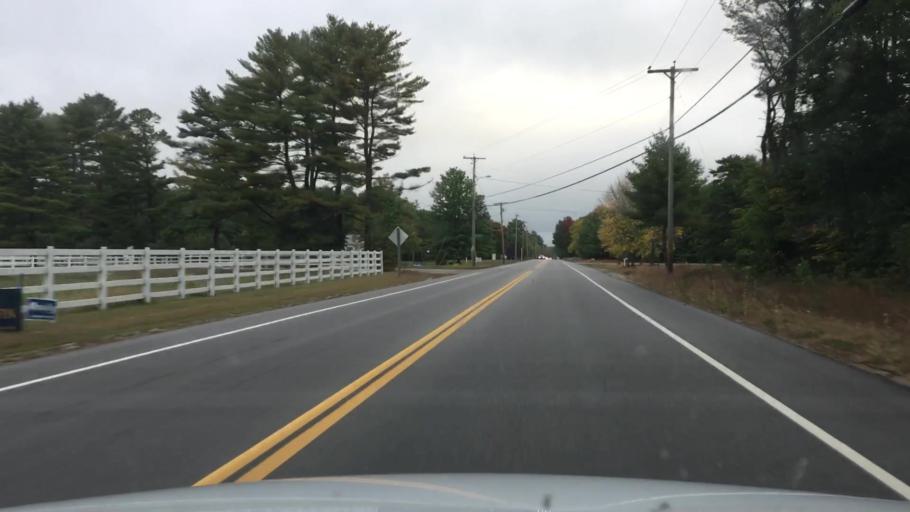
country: US
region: Maine
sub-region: Cumberland County
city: New Gloucester
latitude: 43.9327
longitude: -70.3524
